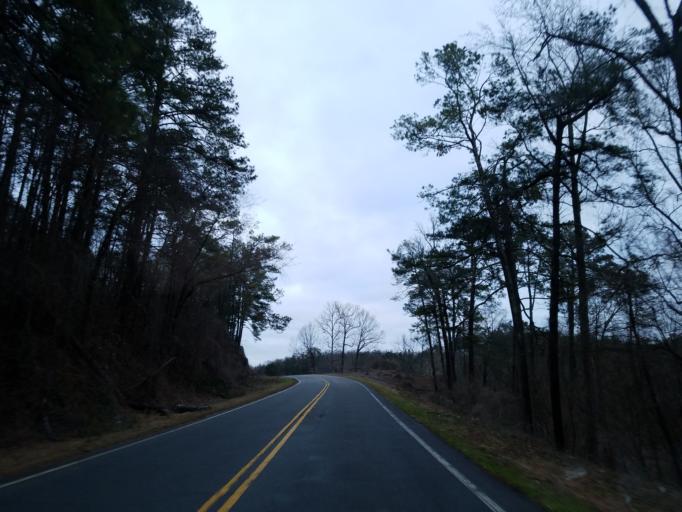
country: US
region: Georgia
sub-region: Bartow County
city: Emerson
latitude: 34.1043
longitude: -84.7421
